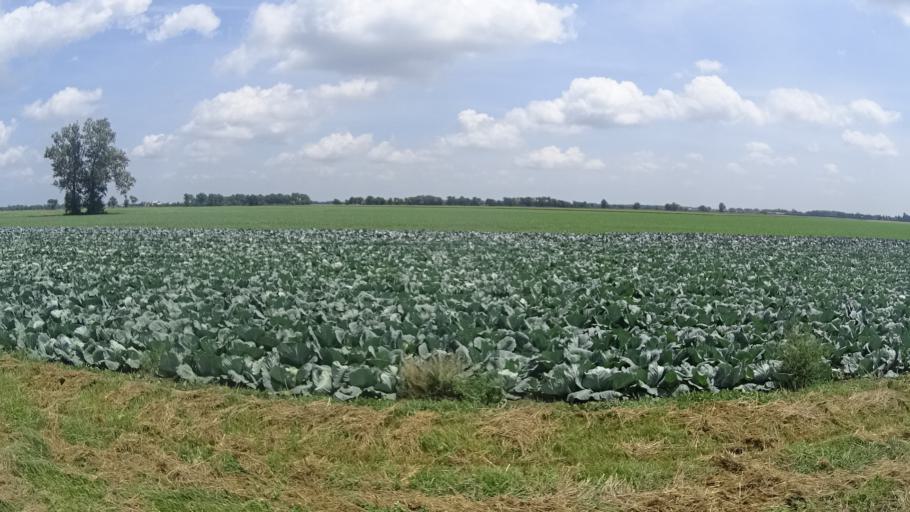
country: US
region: Ohio
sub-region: Huron County
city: Bellevue
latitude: 41.3133
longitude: -82.7596
